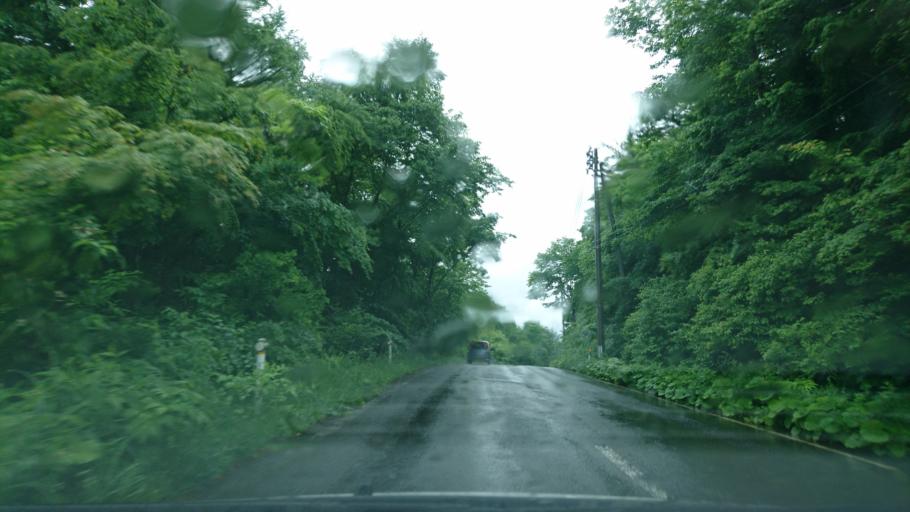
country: JP
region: Iwate
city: Ichinoseki
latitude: 39.0078
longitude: 140.8934
